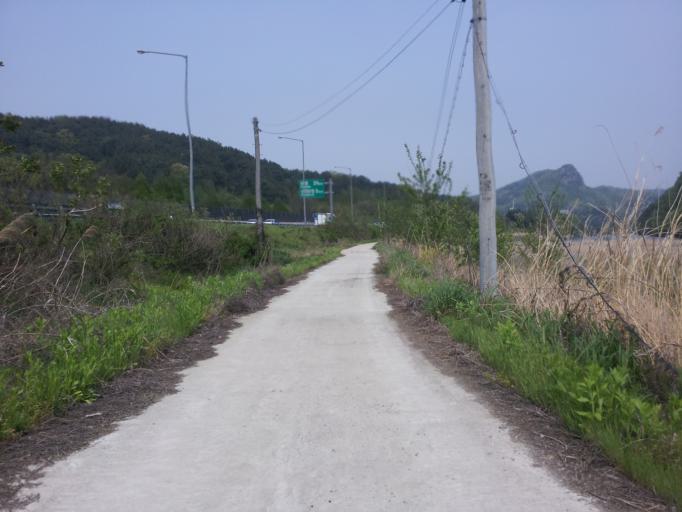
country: KR
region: Daejeon
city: Daejeon
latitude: 36.2586
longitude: 127.2821
